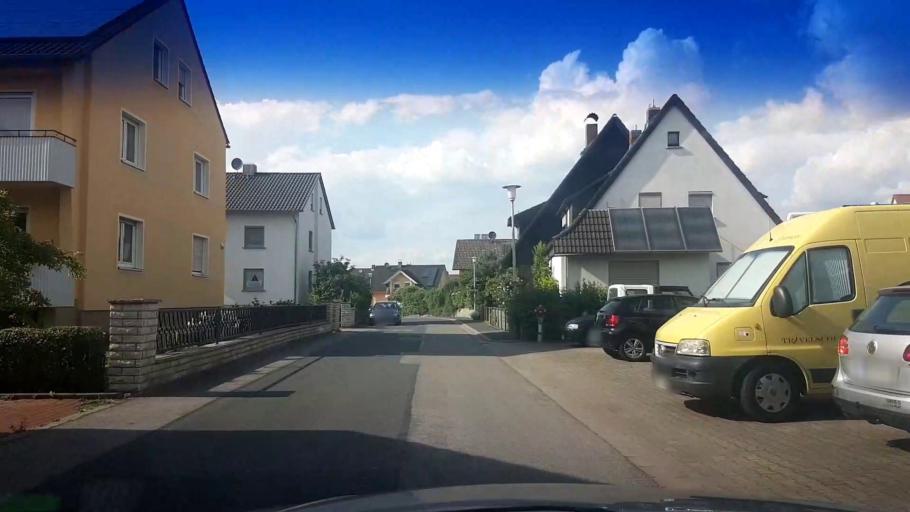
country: DE
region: Bavaria
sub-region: Upper Franconia
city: Breitengussbach
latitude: 49.9688
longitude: 10.8833
